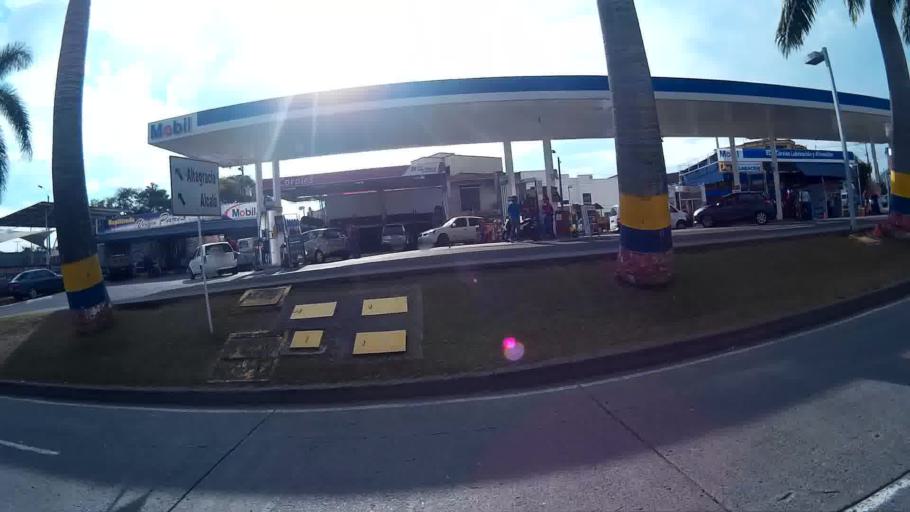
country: CO
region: Risaralda
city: Pereira
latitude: 4.8000
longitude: -75.7428
